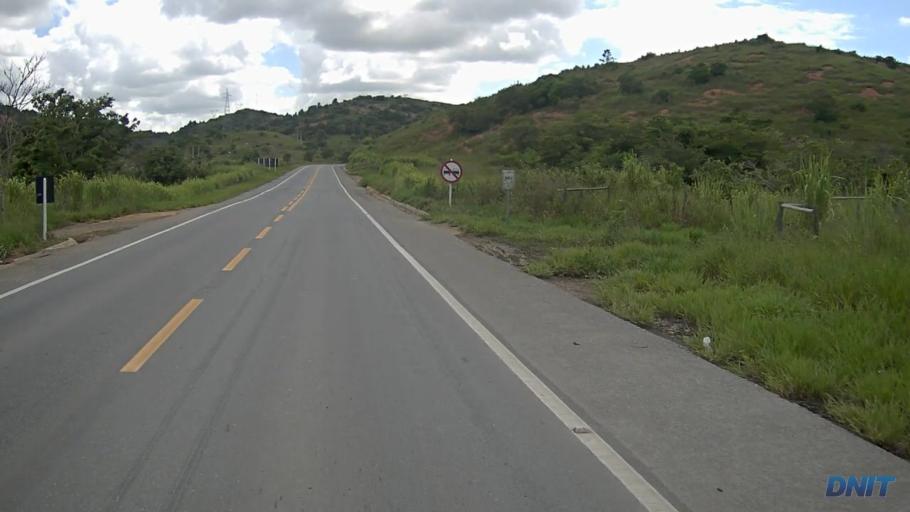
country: BR
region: Minas Gerais
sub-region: Governador Valadares
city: Governador Valadares
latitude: -18.9694
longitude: -42.0924
